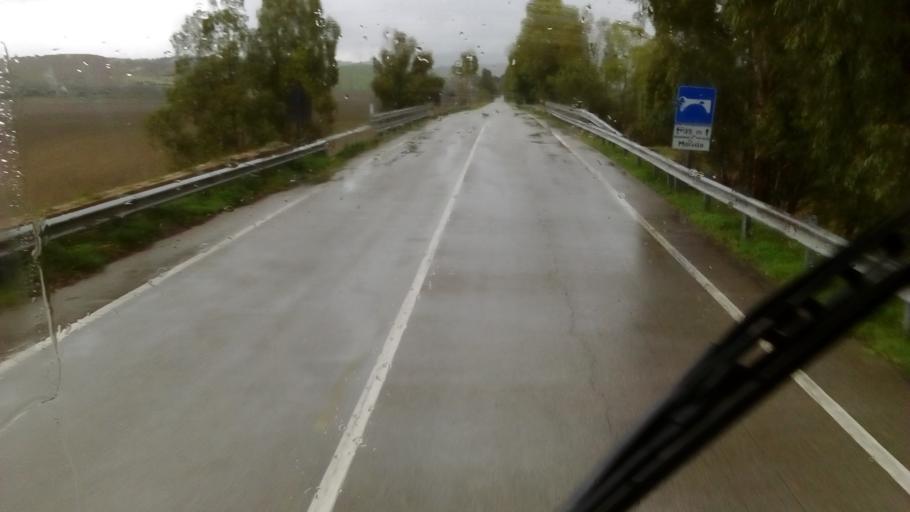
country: IT
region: Sicily
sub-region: Enna
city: Pietraperzia
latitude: 37.4908
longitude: 14.1529
